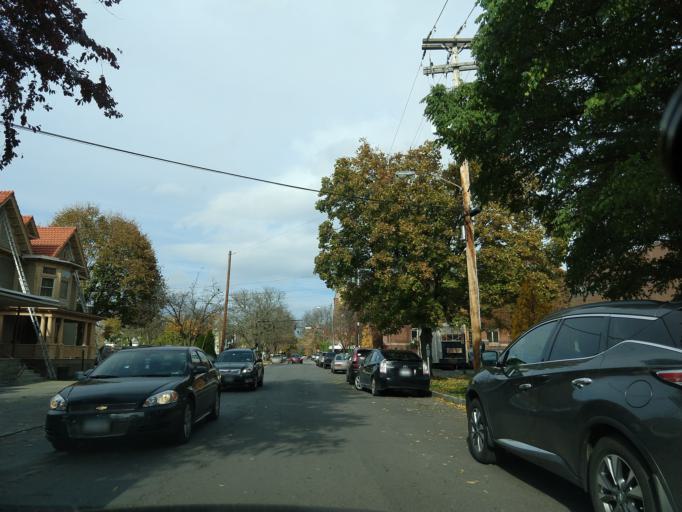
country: US
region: New York
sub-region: Tompkins County
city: Ithaca
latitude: 42.4386
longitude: -76.5007
